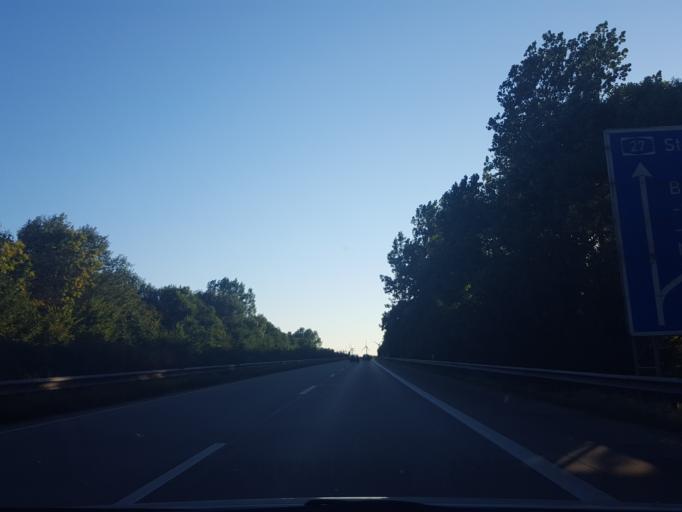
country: DE
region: Lower Saxony
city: Loxstedt
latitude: 53.4698
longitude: 8.6078
